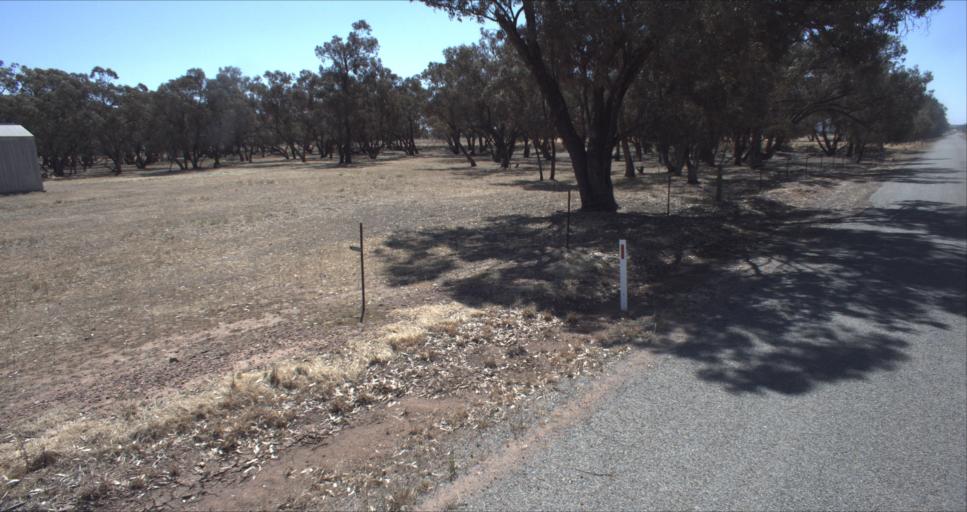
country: AU
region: New South Wales
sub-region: Leeton
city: Leeton
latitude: -34.5007
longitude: 146.4204
